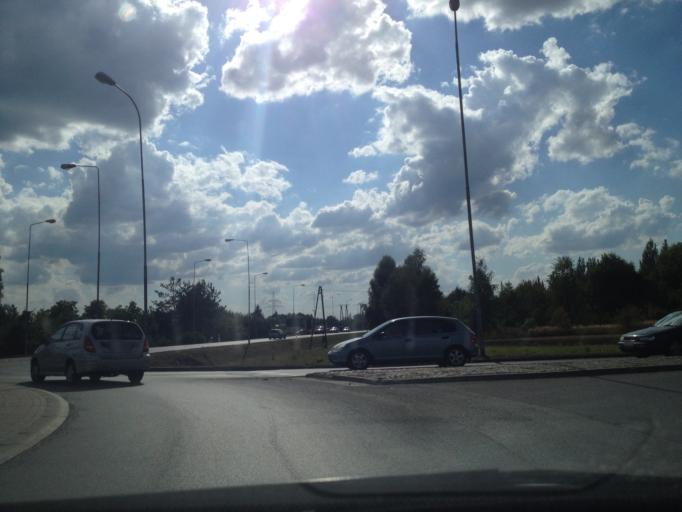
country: PL
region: Lubusz
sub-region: Powiat zarski
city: Zary
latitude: 51.6349
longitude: 15.1182
